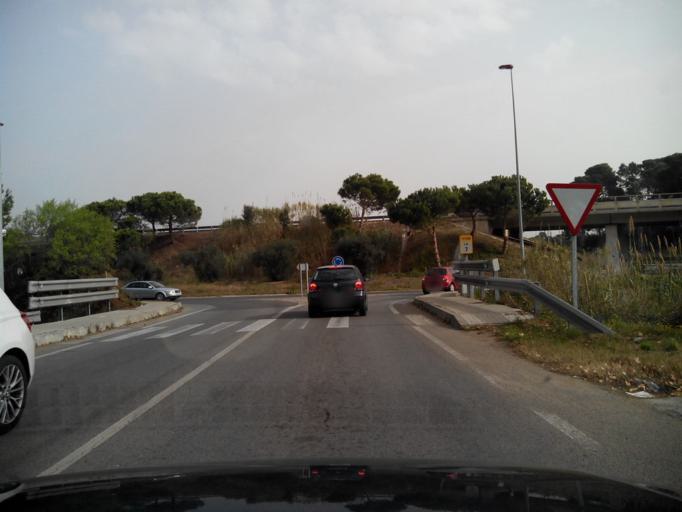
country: ES
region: Catalonia
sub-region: Provincia de Tarragona
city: Reus
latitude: 41.1390
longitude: 1.0979
